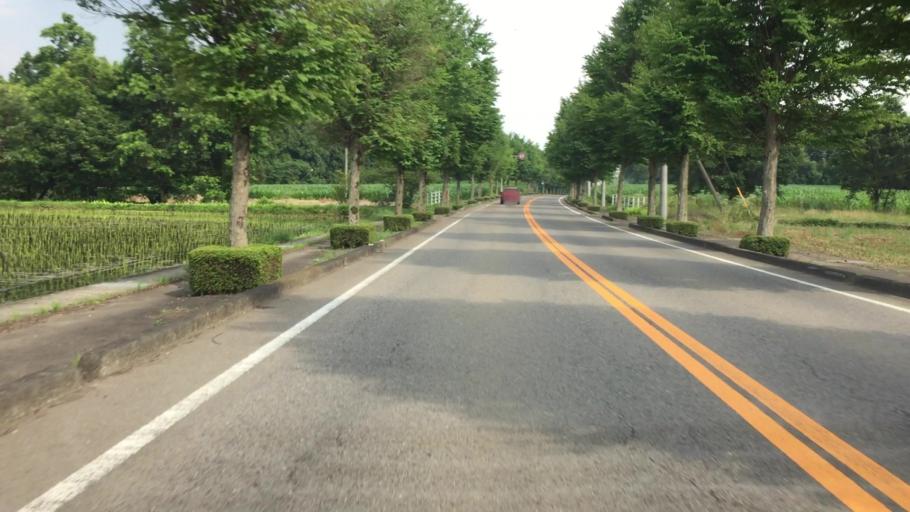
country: JP
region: Tochigi
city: Kuroiso
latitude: 36.9855
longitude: 139.9572
